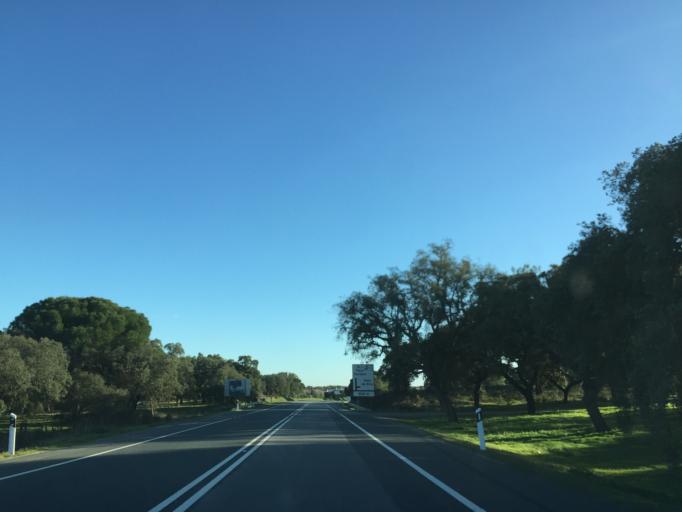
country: PT
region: Setubal
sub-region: Grandola
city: Grandola
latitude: 38.0580
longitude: -8.4049
